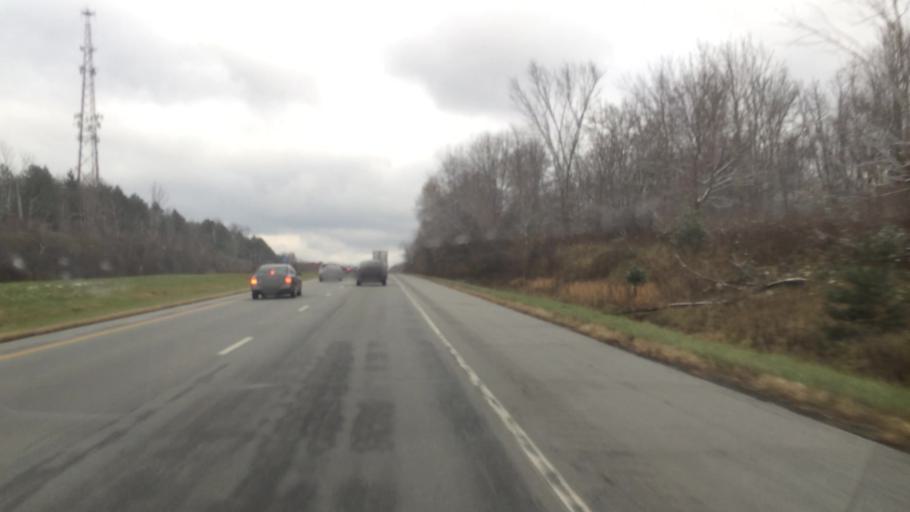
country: US
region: Ohio
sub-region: Summit County
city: Hudson
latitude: 41.2740
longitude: -81.4062
